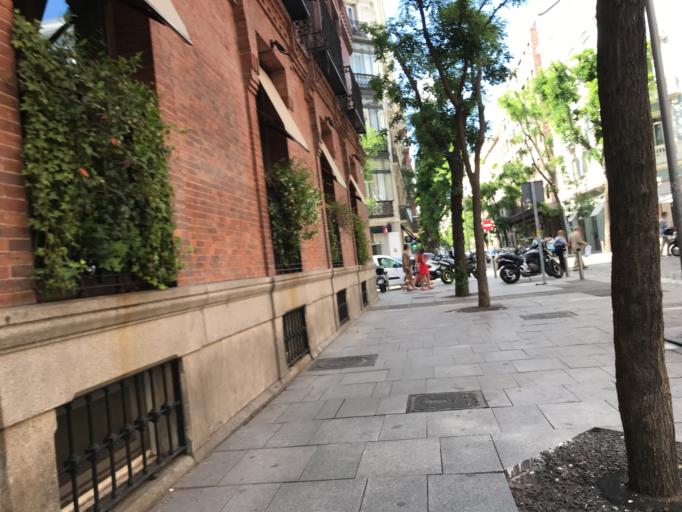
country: ES
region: Madrid
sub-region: Provincia de Madrid
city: Salamanca
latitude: 40.4235
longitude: -3.6855
